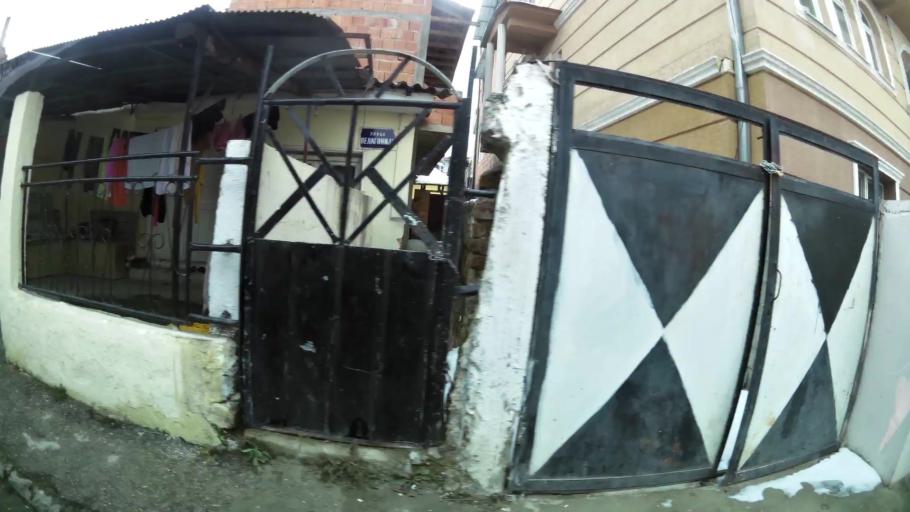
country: MK
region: Suto Orizari
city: Suto Orizare
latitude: 42.0354
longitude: 21.4233
